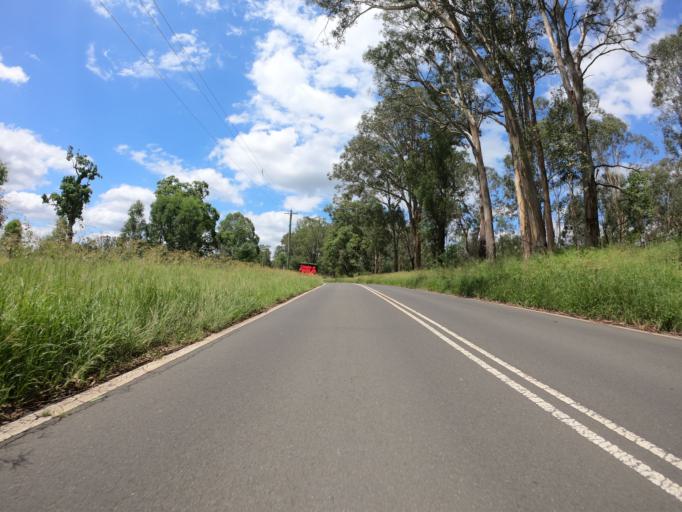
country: AU
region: New South Wales
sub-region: Penrith Municipality
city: Mulgoa
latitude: -33.8301
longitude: 150.6618
